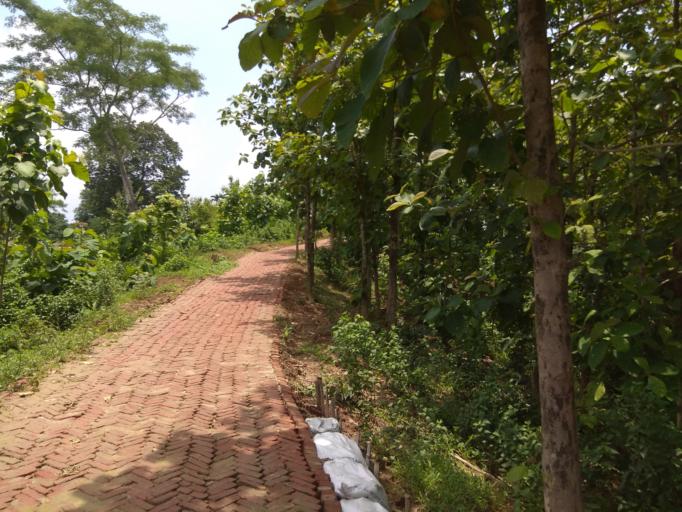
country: BD
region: Chittagong
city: Manikchari
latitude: 22.8859
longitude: 91.9227
